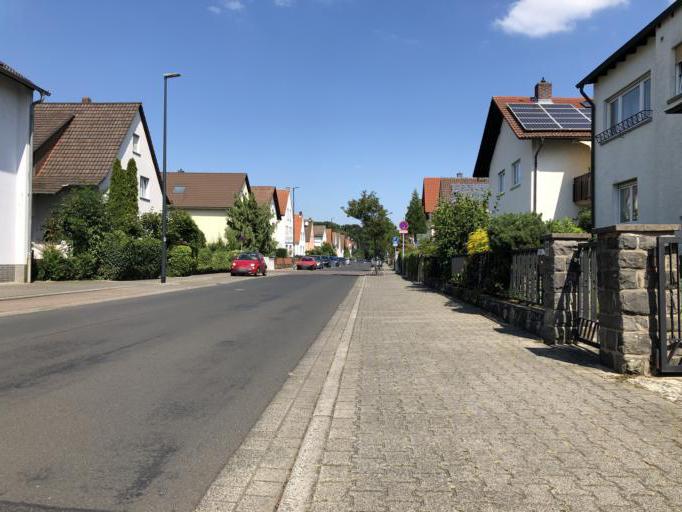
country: DE
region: Hesse
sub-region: Regierungsbezirk Darmstadt
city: Grosskrotzenburg
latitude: 50.0849
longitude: 8.9815
